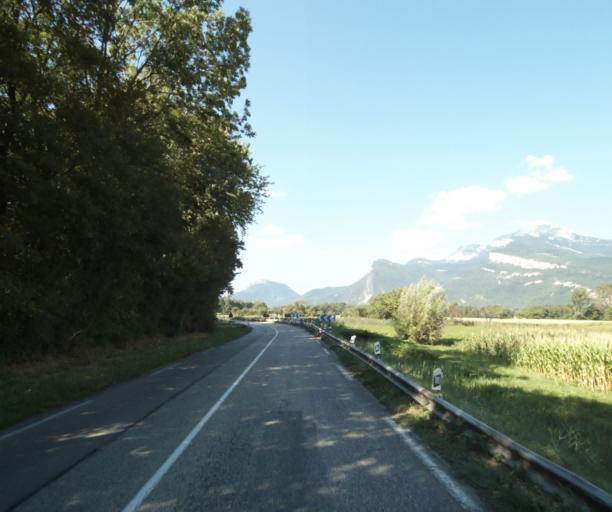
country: FR
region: Rhone-Alpes
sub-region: Departement de l'Isere
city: Noyarey
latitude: 45.2466
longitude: 5.6330
